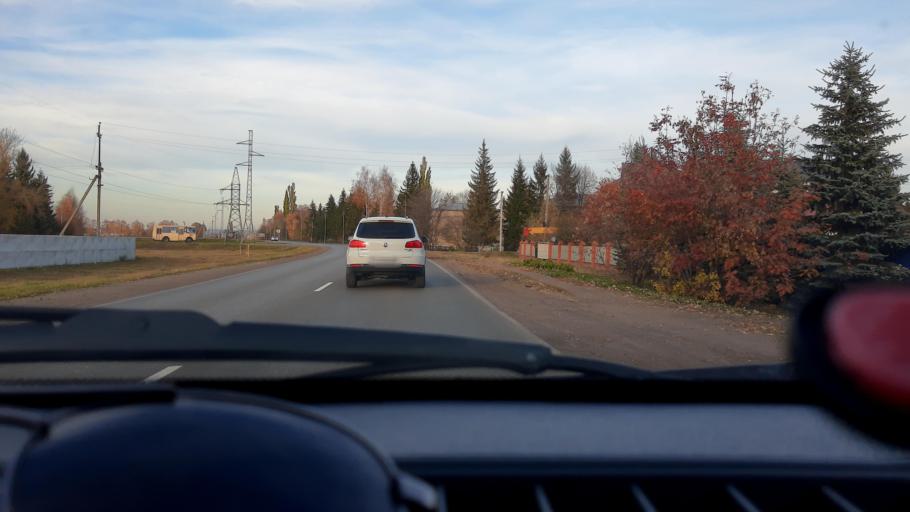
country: RU
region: Bashkortostan
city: Ufa
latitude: 54.8271
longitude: 55.9927
